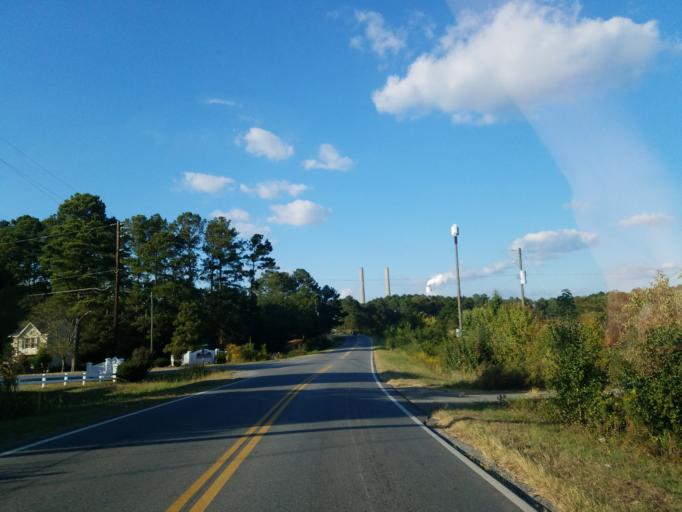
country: US
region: Georgia
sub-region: Bartow County
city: Euharlee
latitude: 34.1027
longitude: -84.9268
